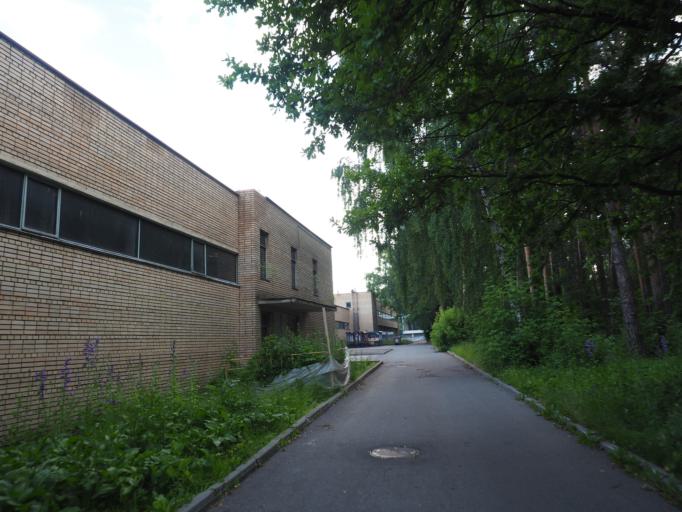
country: RU
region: Moscow
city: Ostankinskiy
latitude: 55.8404
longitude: 37.6197
